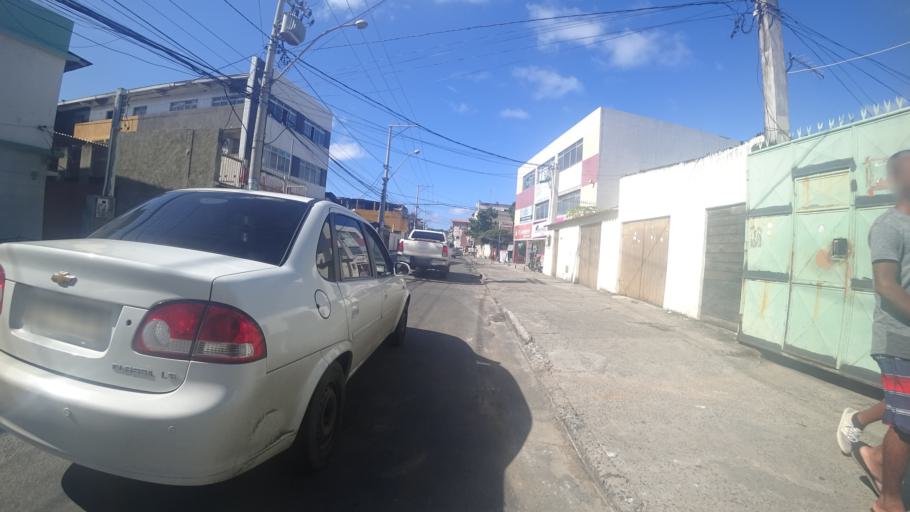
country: BR
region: Bahia
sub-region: Salvador
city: Salvador
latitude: -12.9753
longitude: -38.4315
